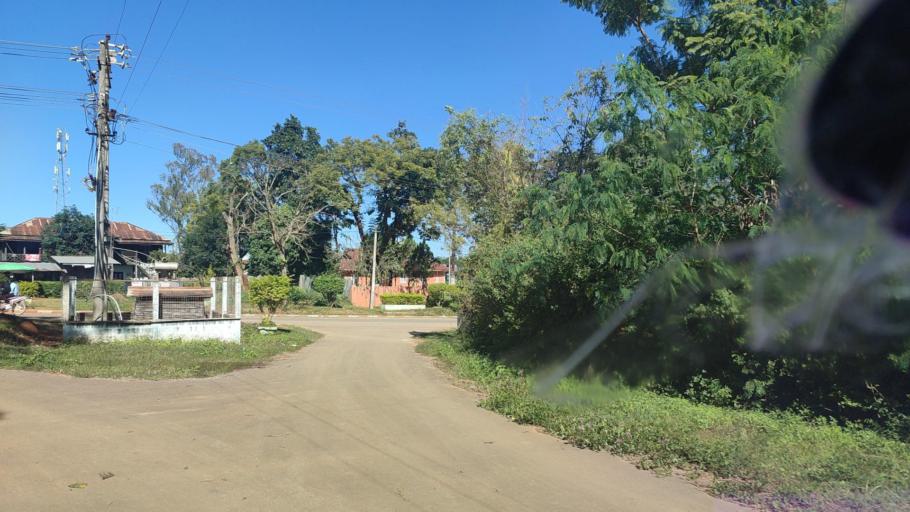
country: MM
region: Shan
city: Taunggyi
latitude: 20.9194
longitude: 97.5692
